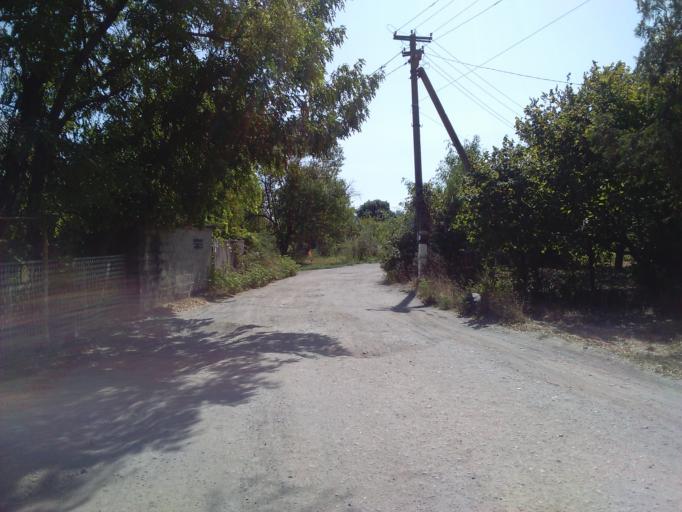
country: RU
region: Rostov
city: Azov
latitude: 47.1330
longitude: 39.4772
